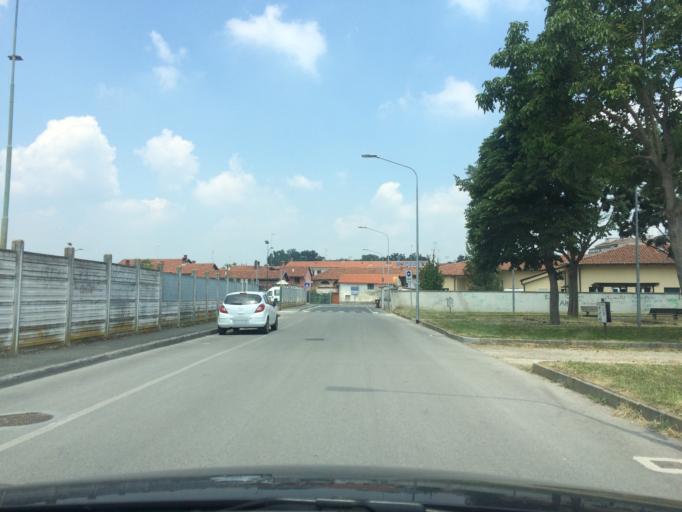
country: IT
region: Piedmont
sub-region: Provincia di Cuneo
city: Racconigi
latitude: 44.7654
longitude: 7.6732
